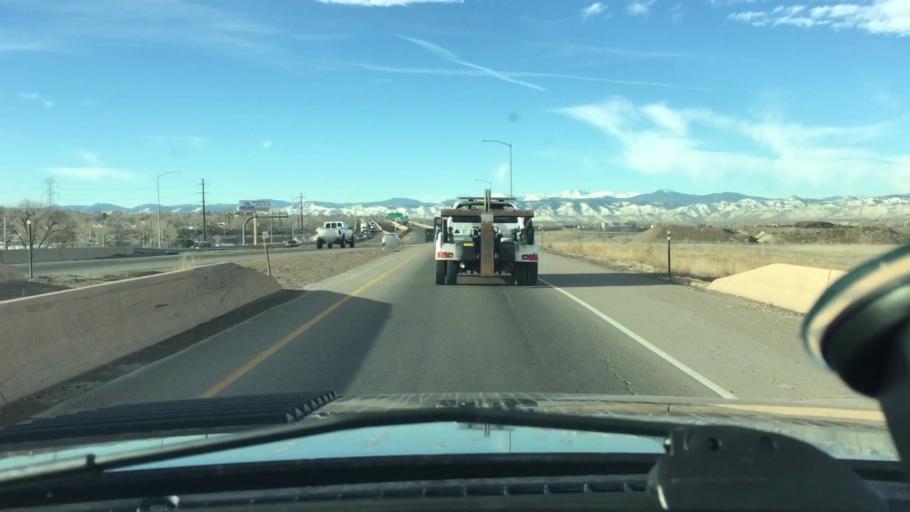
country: US
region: Colorado
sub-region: Adams County
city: Berkley
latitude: 39.8081
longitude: -105.0107
